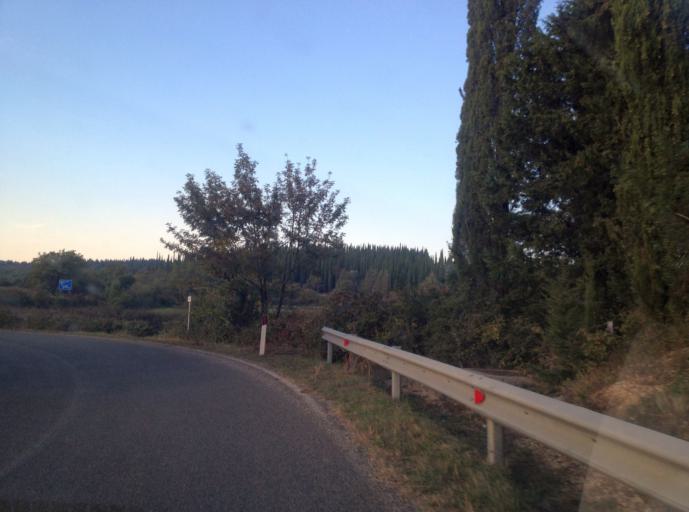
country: IT
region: Tuscany
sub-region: Provincia di Siena
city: Castellina in Chianti
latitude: 43.4404
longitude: 11.3011
